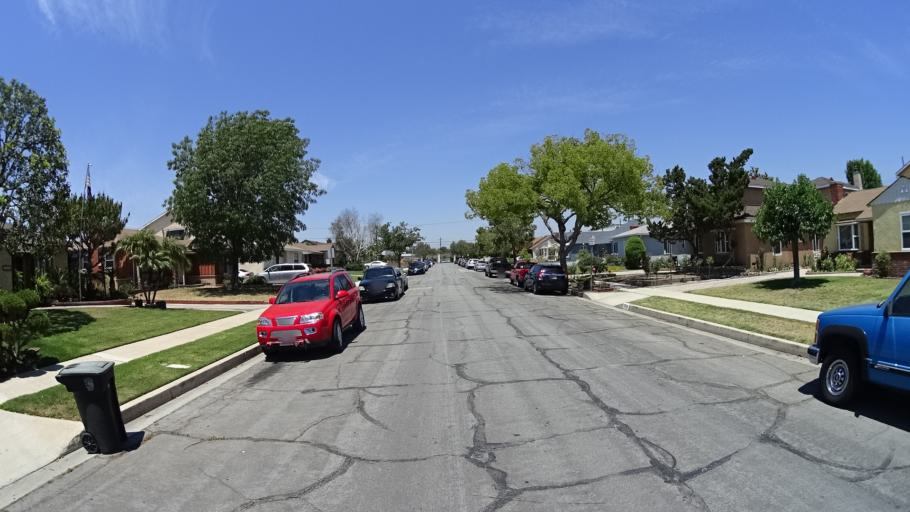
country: US
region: California
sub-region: Los Angeles County
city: North Hollywood
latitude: 34.1749
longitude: -118.3446
